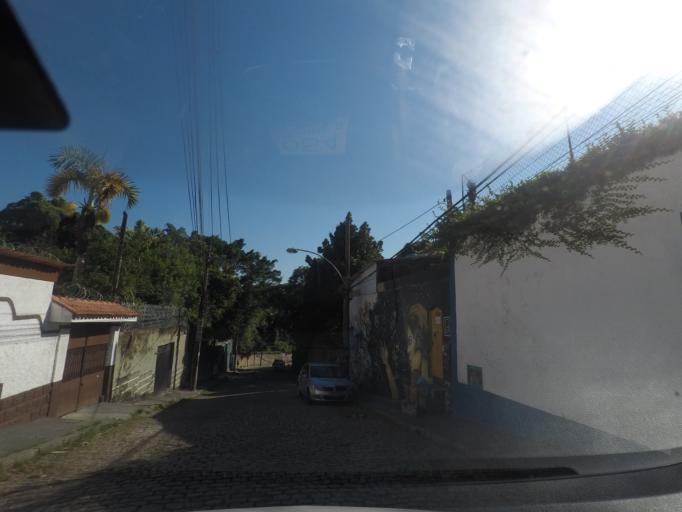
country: BR
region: Rio de Janeiro
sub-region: Rio De Janeiro
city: Rio de Janeiro
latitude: -22.9424
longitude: -43.2060
